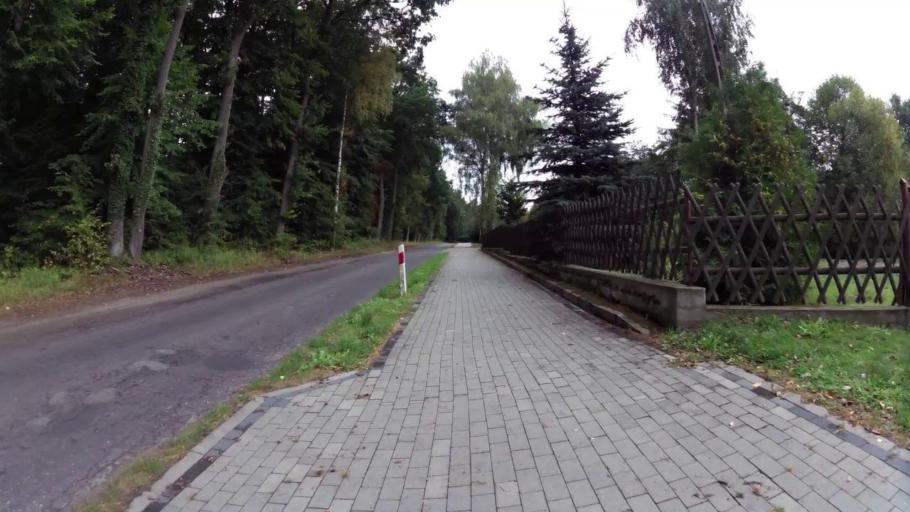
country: PL
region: West Pomeranian Voivodeship
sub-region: Powiat mysliborski
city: Debno
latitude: 52.7598
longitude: 14.6956
